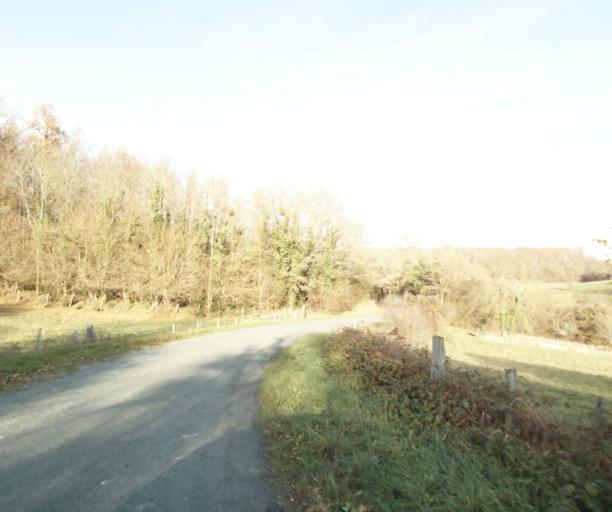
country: FR
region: Poitou-Charentes
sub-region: Departement de la Charente-Maritime
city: Chaniers
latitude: 45.7246
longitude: -0.5352
